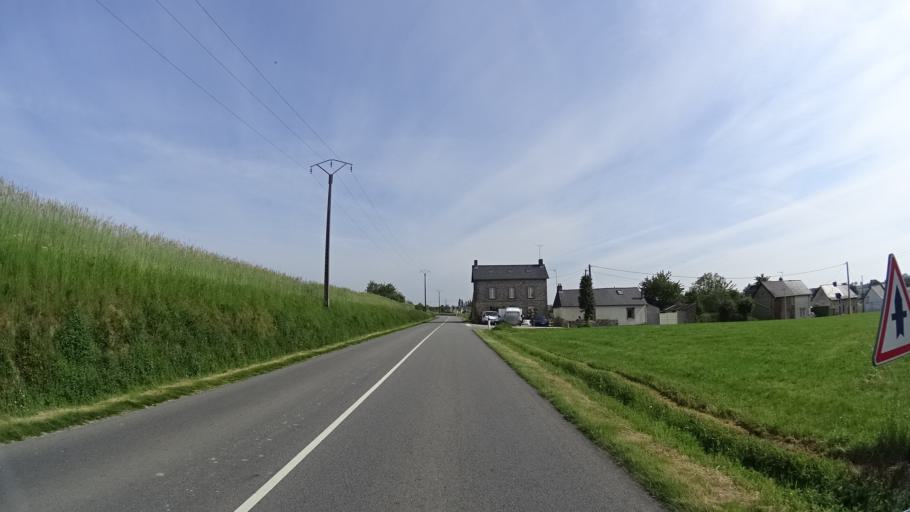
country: FR
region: Brittany
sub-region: Departement d'Ille-et-Vilaine
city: Chateaugiron
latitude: 48.0274
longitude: -1.5058
